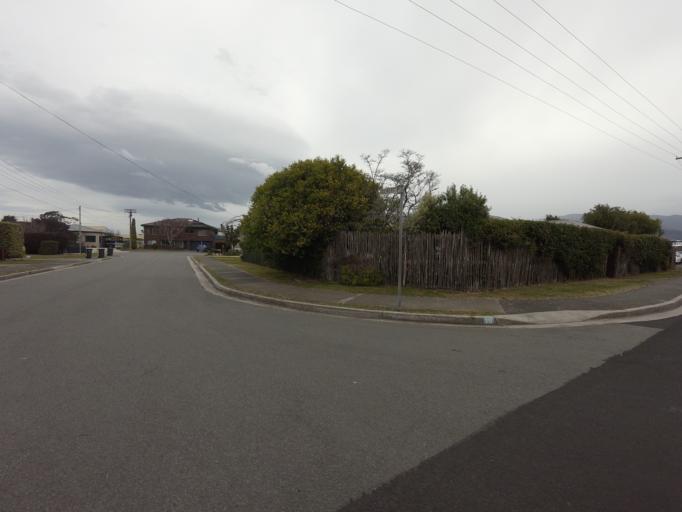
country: AU
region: Tasmania
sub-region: Clarence
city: Bellerive
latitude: -42.8773
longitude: 147.3842
